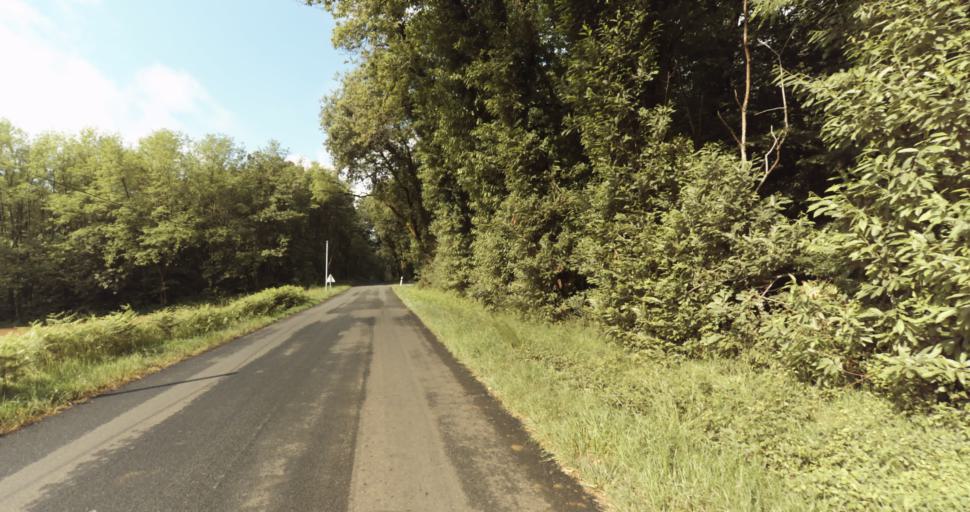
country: FR
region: Aquitaine
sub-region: Departement de la Dordogne
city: Lalinde
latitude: 44.9070
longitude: 0.7815
